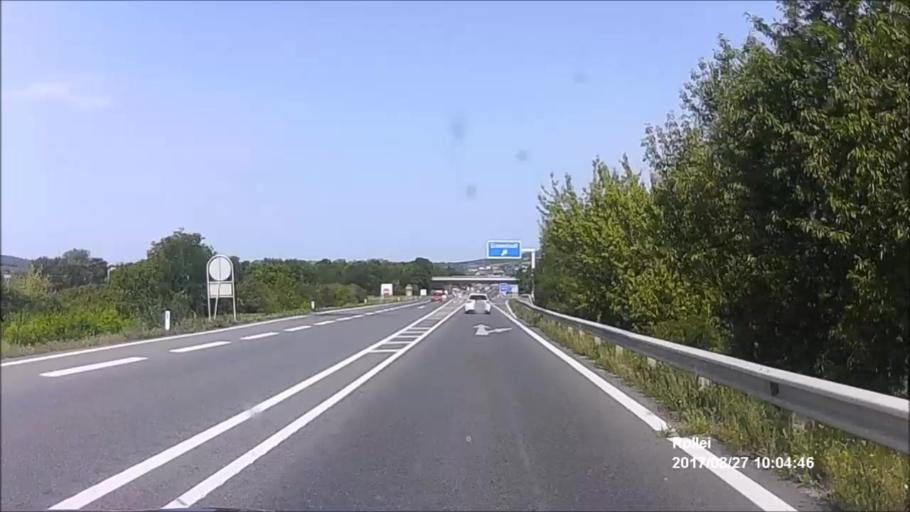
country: AT
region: Burgenland
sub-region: Eisenstadt-Umgebung
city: Wulkaprodersdorf
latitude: 47.8099
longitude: 16.5011
